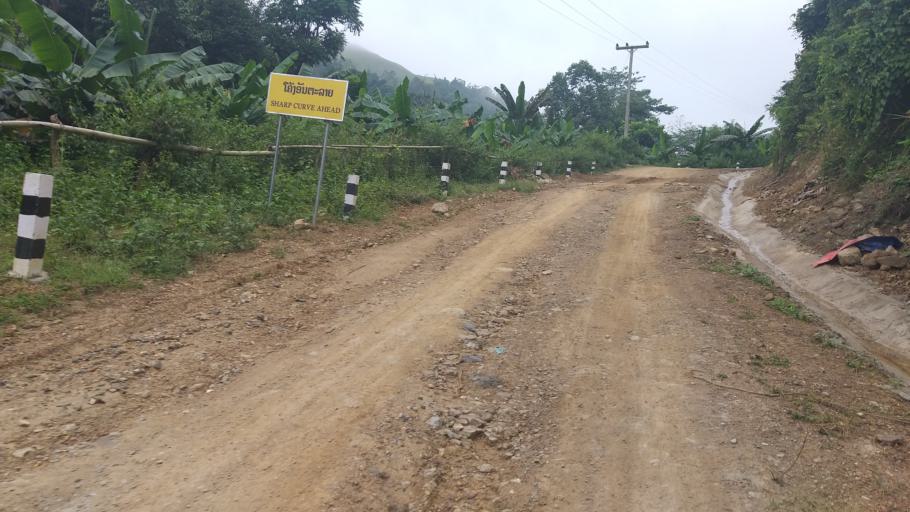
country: LA
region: Phongsali
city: Khoa
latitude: 21.2388
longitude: 102.6707
